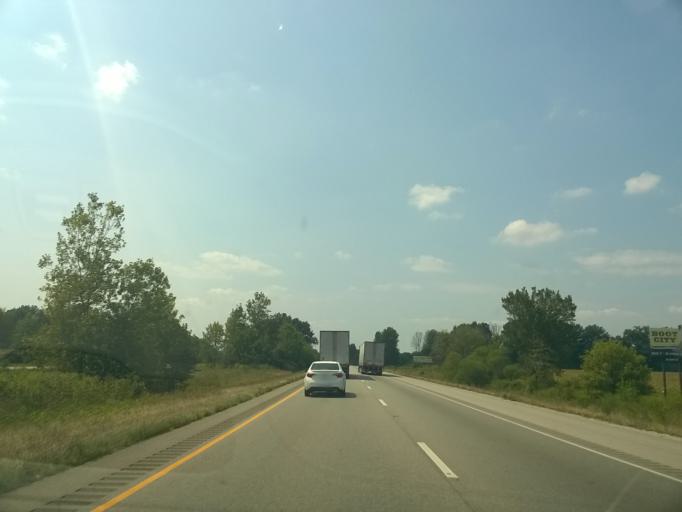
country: US
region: Indiana
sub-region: Vigo County
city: Seelyville
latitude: 39.4458
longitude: -87.2554
